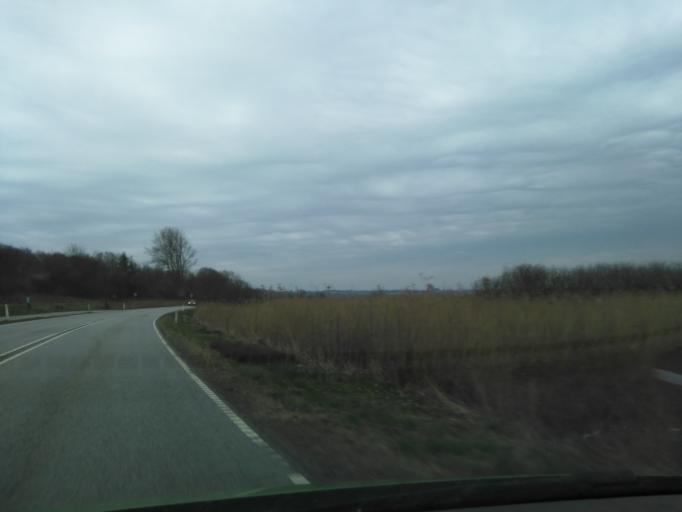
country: DK
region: North Denmark
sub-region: Mariagerfjord Kommune
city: Hadsund
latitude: 56.6953
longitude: 10.1115
